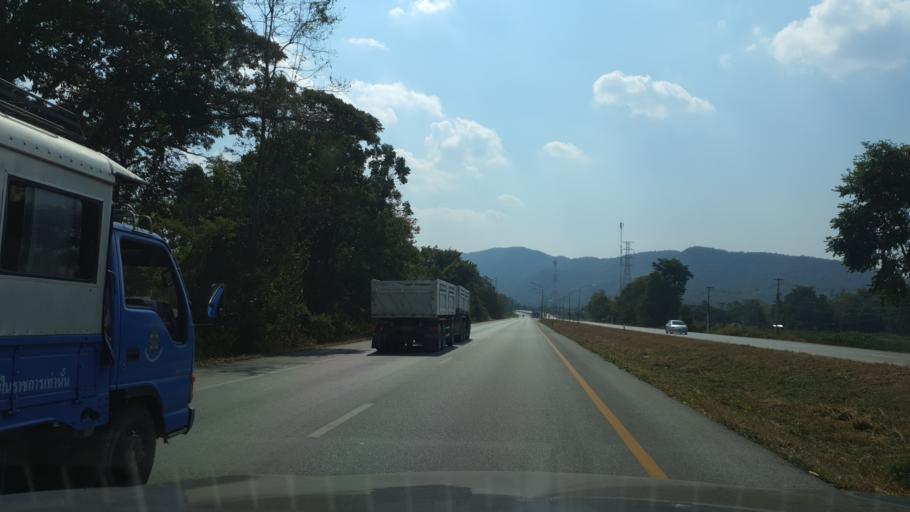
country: TH
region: Lampang
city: Mae Phrik
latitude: 17.3713
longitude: 99.1485
